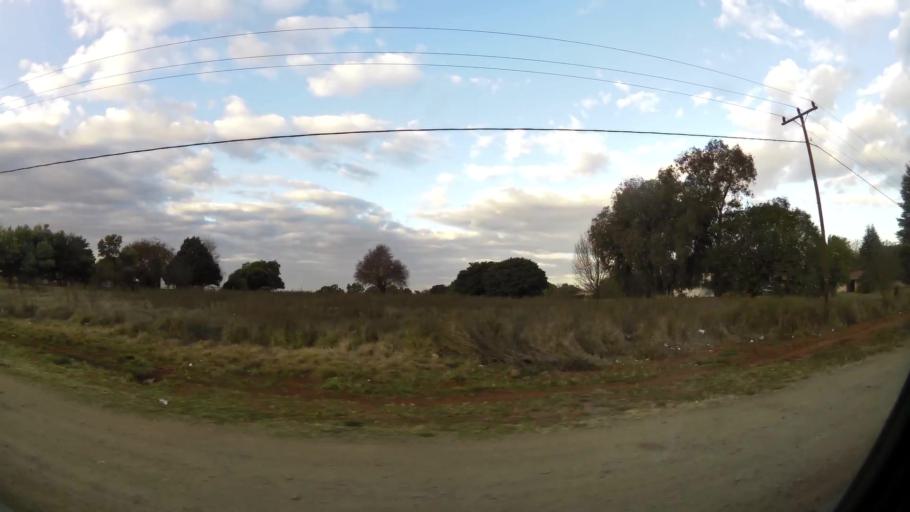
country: ZA
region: Gauteng
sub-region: City of Johannesburg Metropolitan Municipality
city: Midrand
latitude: -26.0041
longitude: 28.1577
